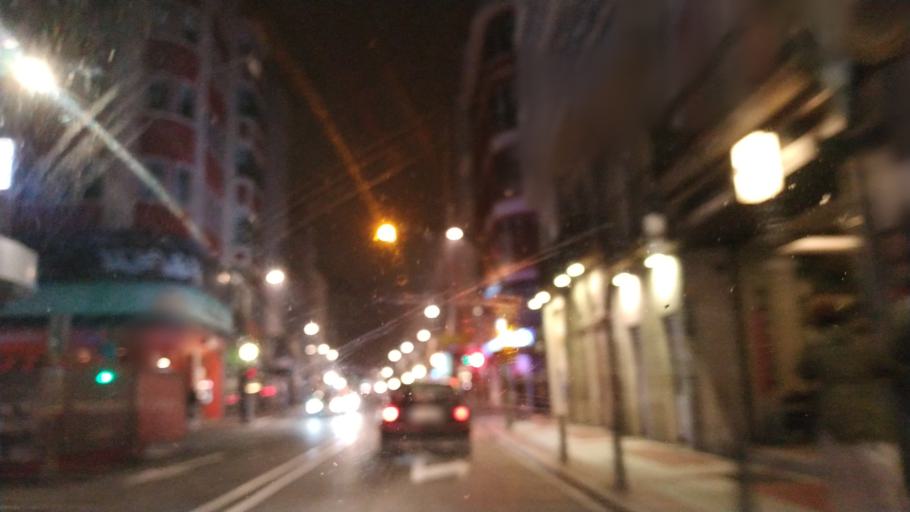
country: ES
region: Galicia
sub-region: Provincia da Coruna
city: A Coruna
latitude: 43.3699
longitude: -8.4031
